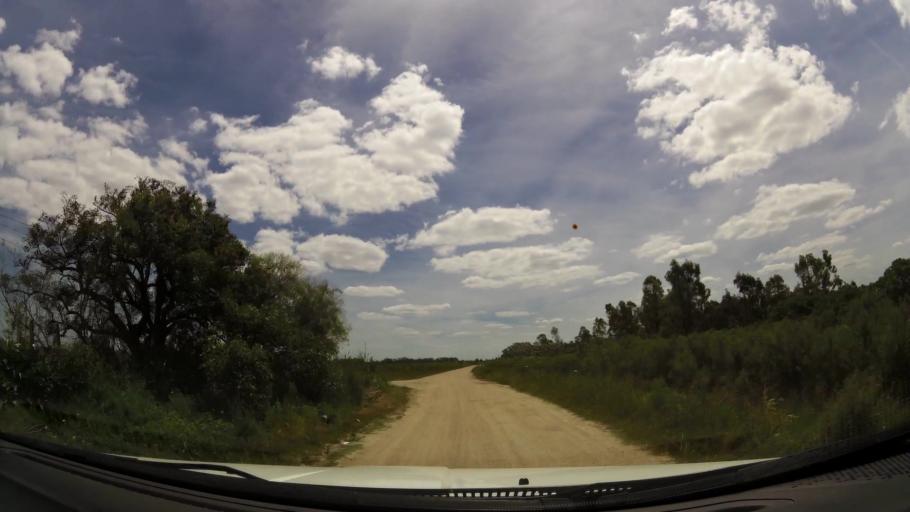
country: UY
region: San Jose
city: Delta del Tigre
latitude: -34.7505
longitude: -56.4238
